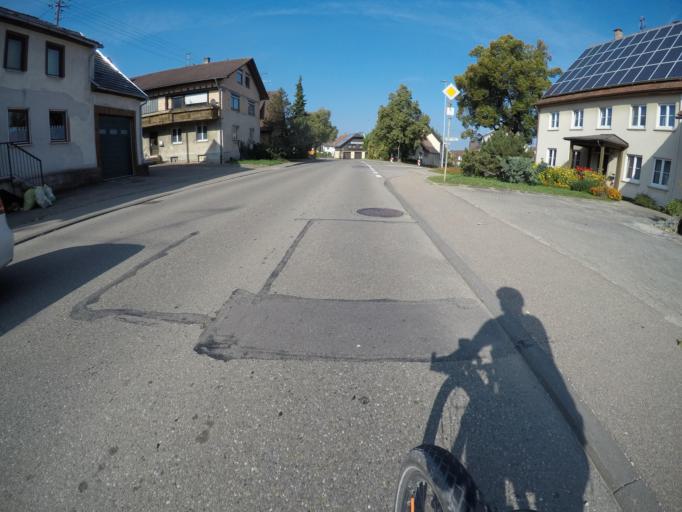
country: DE
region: Baden-Wuerttemberg
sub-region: Regierungsbezirk Stuttgart
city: Bohmenkirch
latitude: 48.6409
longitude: 9.9601
